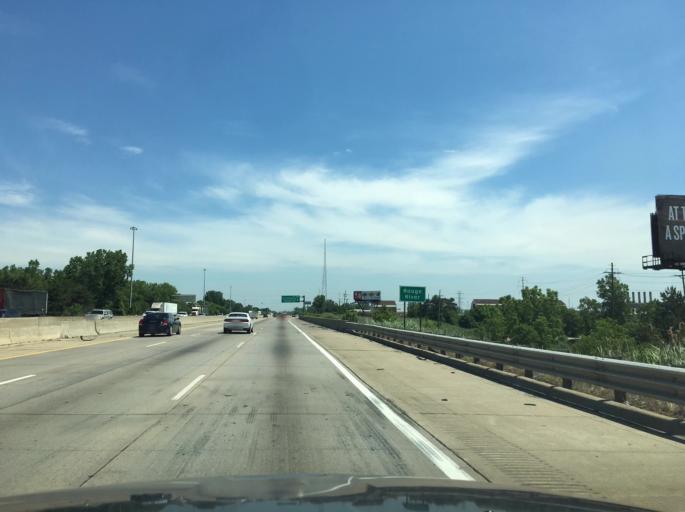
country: US
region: Michigan
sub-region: Wayne County
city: Melvindale
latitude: 42.2943
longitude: -83.1882
